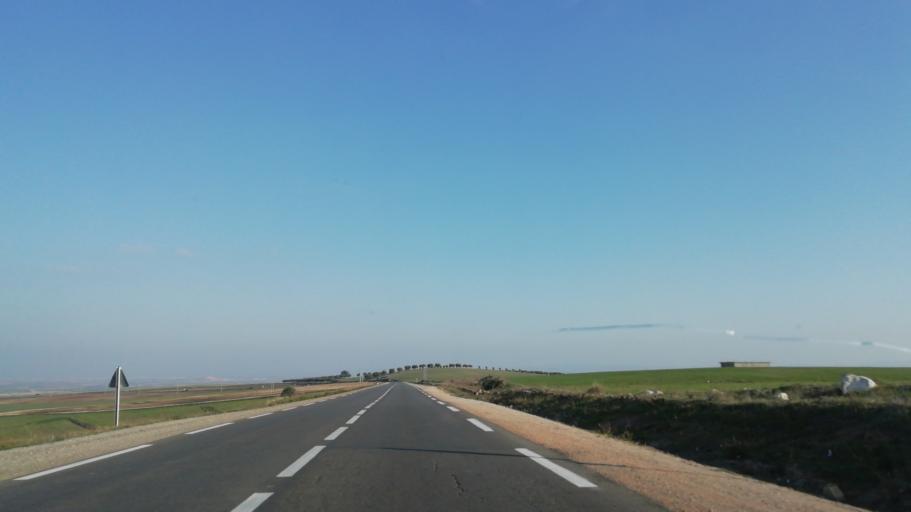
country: DZ
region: Sidi Bel Abbes
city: Sidi Bel Abbes
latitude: 35.1652
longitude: -0.8576
